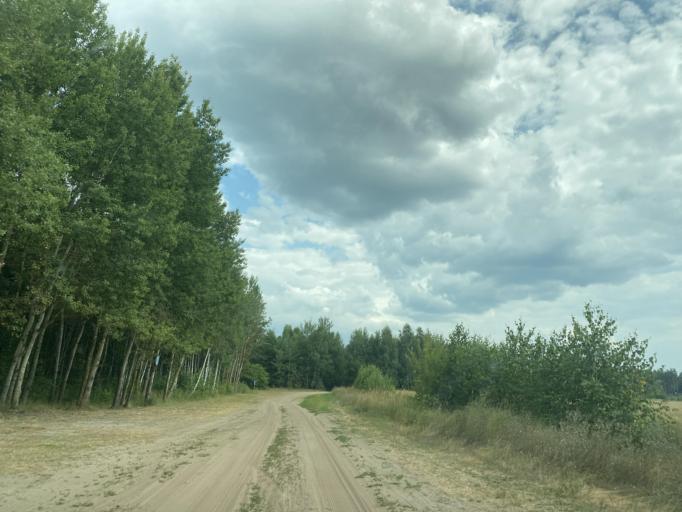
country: BY
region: Brest
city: Ivanava
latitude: 52.3664
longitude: 25.6333
